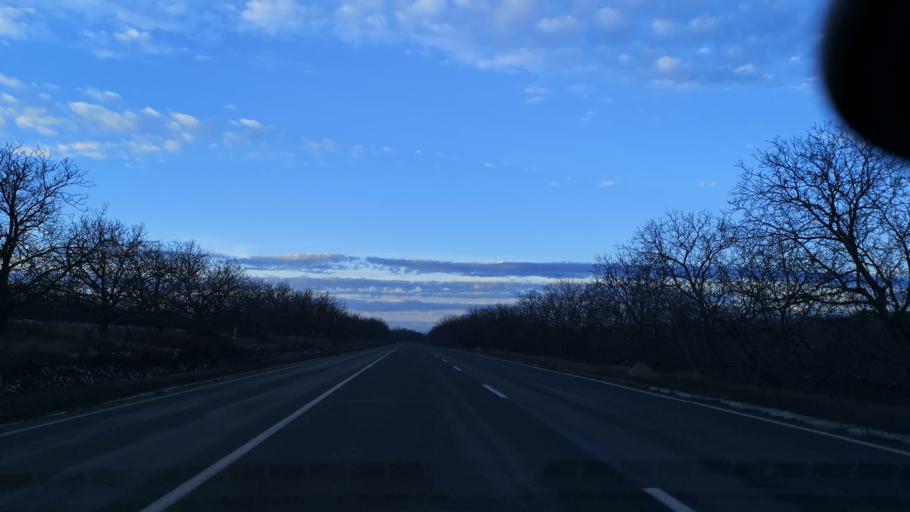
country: MD
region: Orhei
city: Orhei
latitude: 47.5139
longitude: 28.7995
